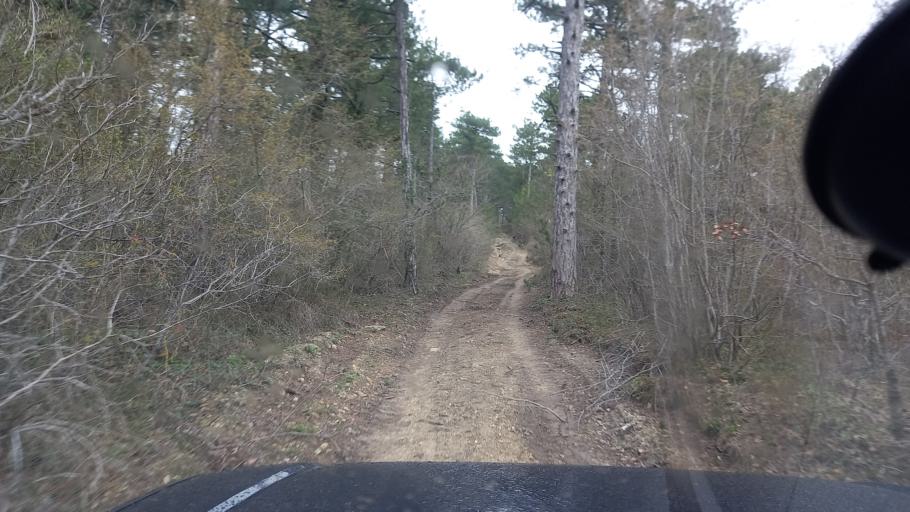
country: RU
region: Krasnodarskiy
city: Arkhipo-Osipovka
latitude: 44.3718
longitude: 38.4729
